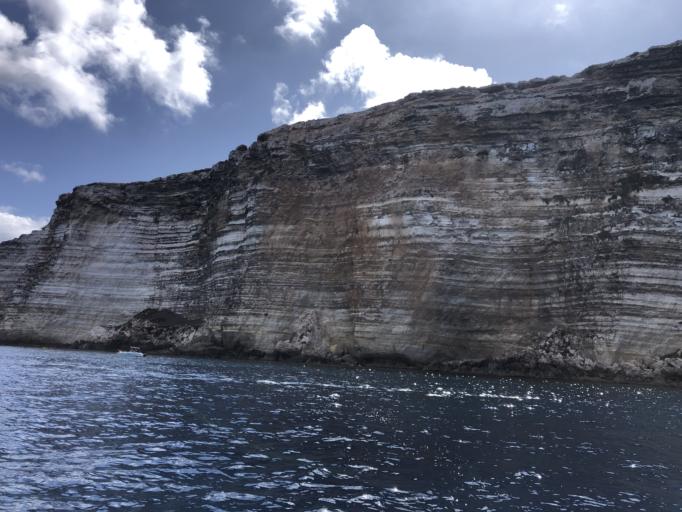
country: IT
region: Sicily
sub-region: Agrigento
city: Lampedusa
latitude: 35.5246
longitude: 12.5202
